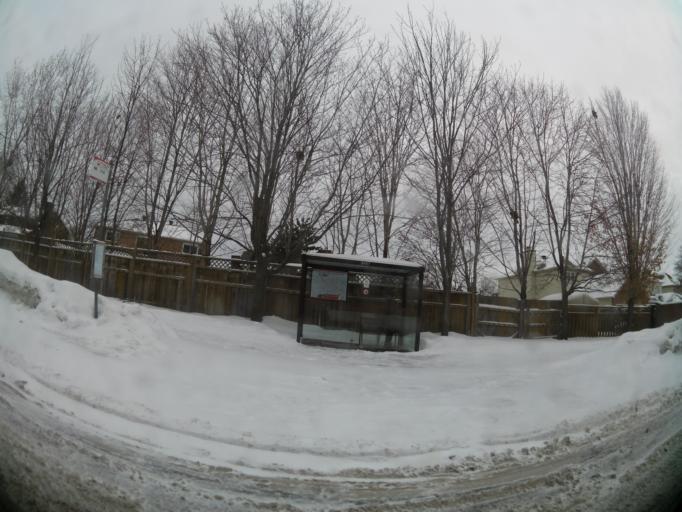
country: CA
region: Ontario
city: Ottawa
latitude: 45.3730
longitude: -75.6111
